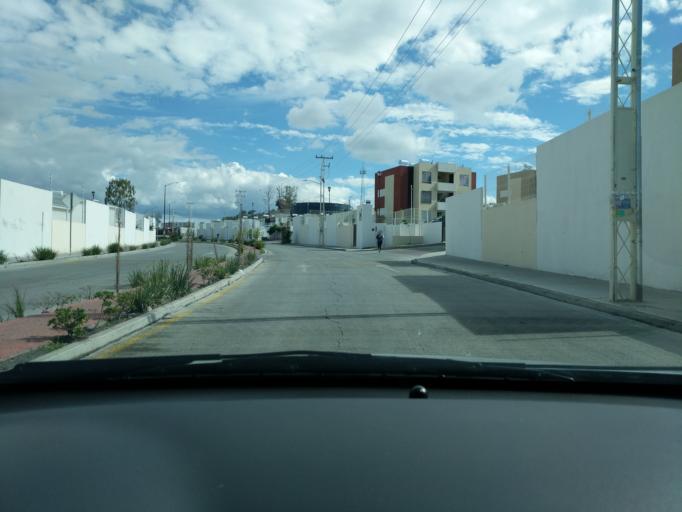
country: MX
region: Queretaro
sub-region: El Marques
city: La Loma
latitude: 20.5874
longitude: -100.2625
